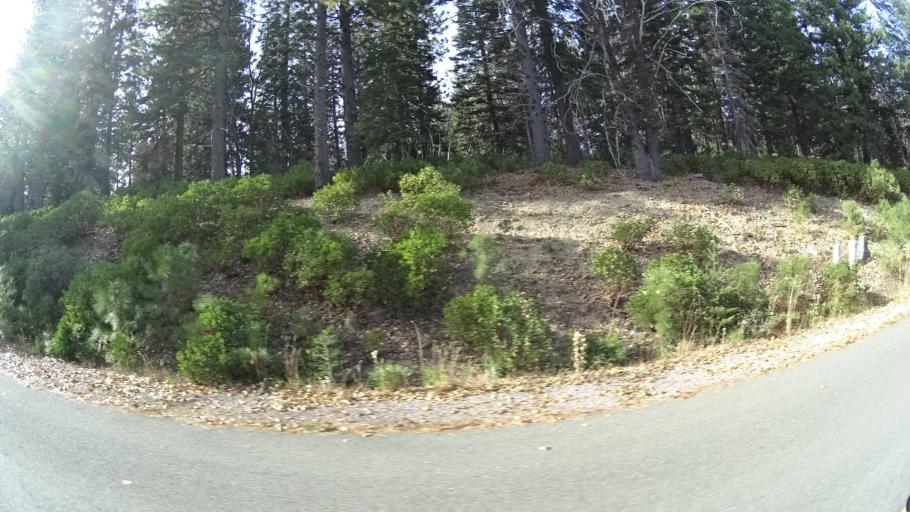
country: US
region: California
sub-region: Siskiyou County
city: Weed
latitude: 41.3953
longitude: -122.3928
